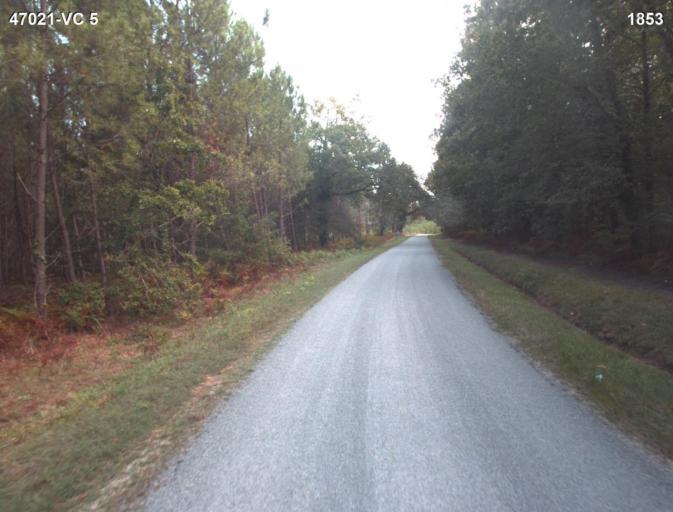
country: FR
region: Aquitaine
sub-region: Departement du Lot-et-Garonne
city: Barbaste
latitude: 44.1435
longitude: 0.2752
